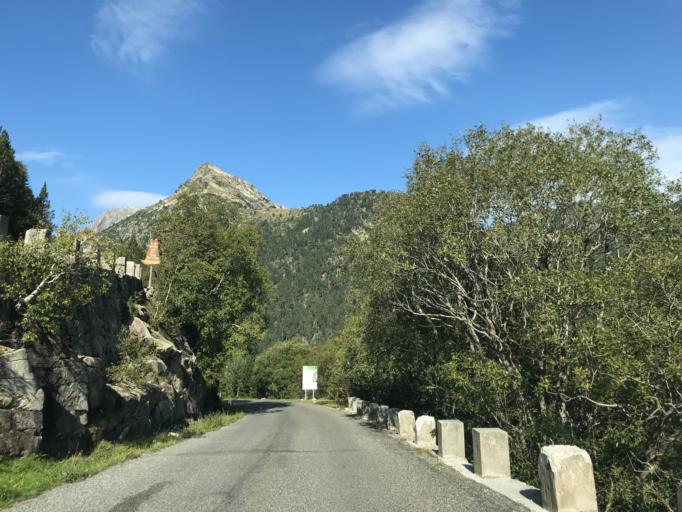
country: FR
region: Midi-Pyrenees
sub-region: Departement des Hautes-Pyrenees
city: Saint-Lary-Soulan
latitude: 42.8244
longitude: 0.1690
